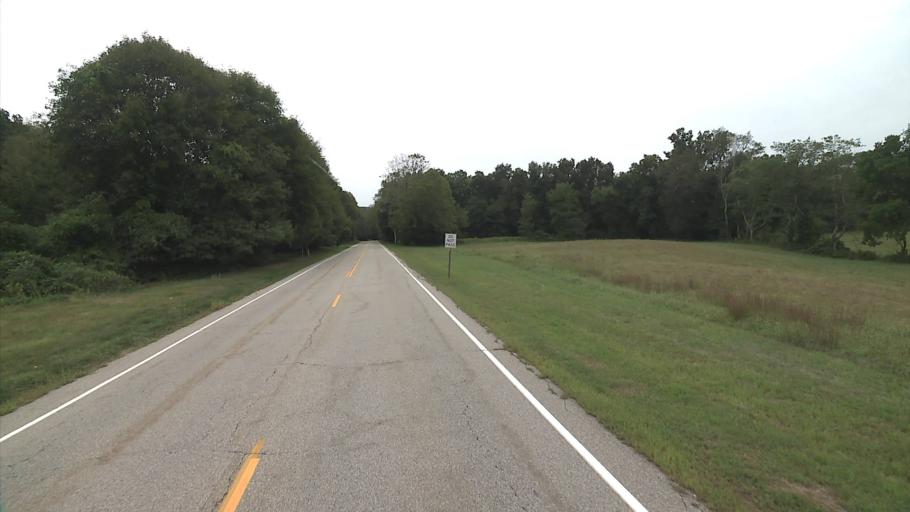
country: US
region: Connecticut
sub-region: Middlesex County
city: Essex Village
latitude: 41.4220
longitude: -72.3346
